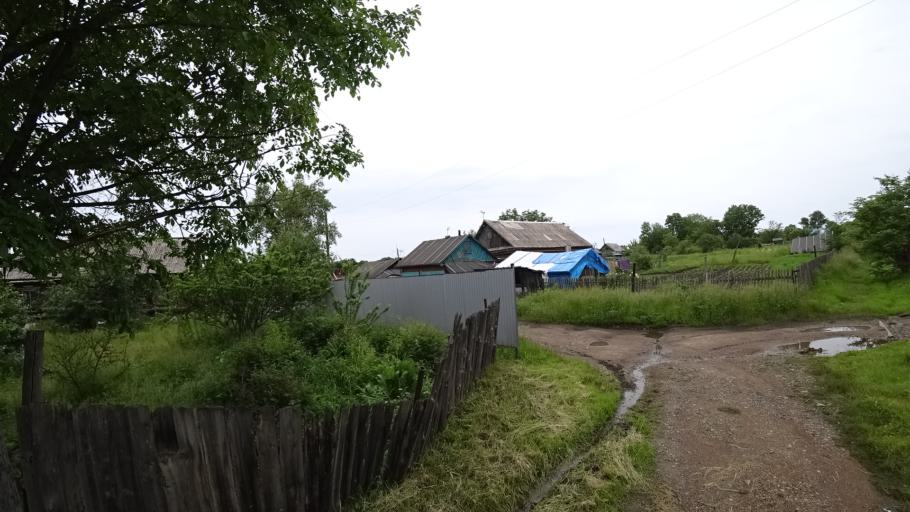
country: RU
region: Primorskiy
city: Novosysoyevka
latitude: 44.2078
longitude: 133.3353
